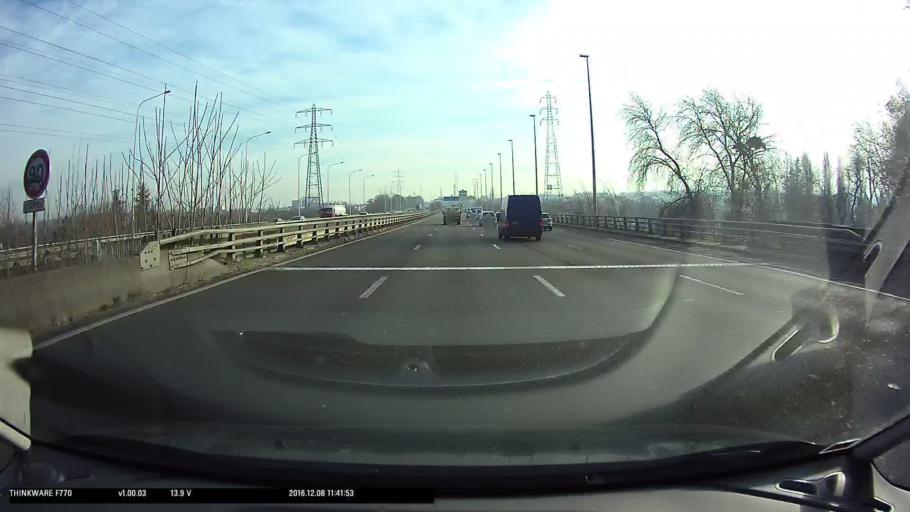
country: FR
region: Ile-de-France
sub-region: Departement du Val-d'Oise
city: Pontoise
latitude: 49.0363
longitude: 2.0943
